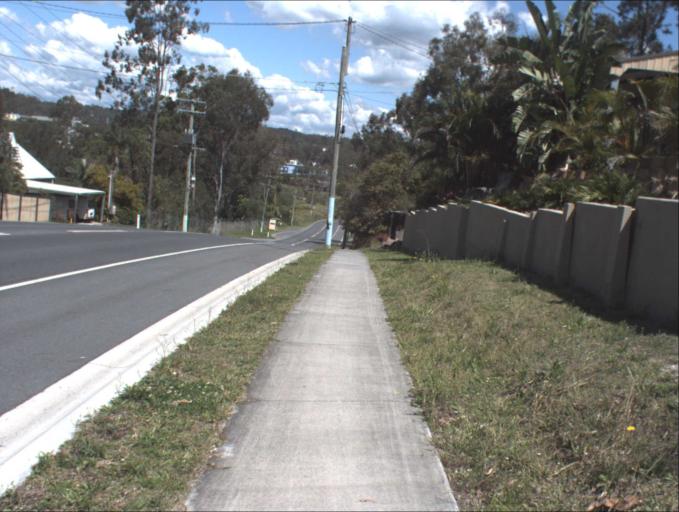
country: AU
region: Queensland
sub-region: Logan
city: Beenleigh
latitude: -27.7088
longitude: 153.1814
